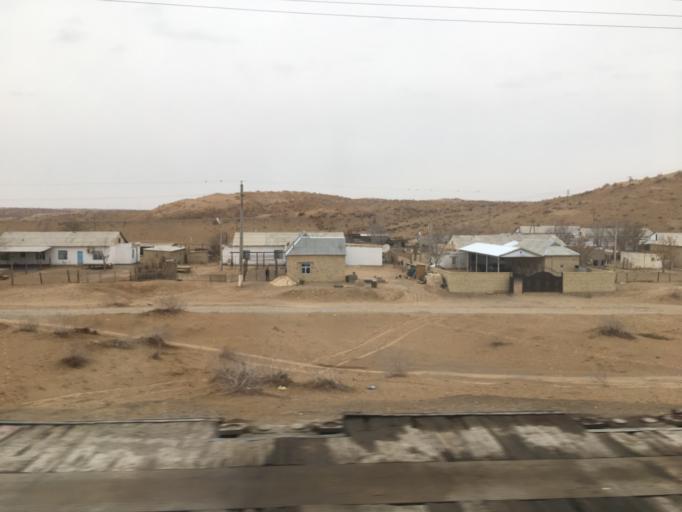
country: TM
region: Mary
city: Yoloeten
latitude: 36.4615
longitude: 62.5936
